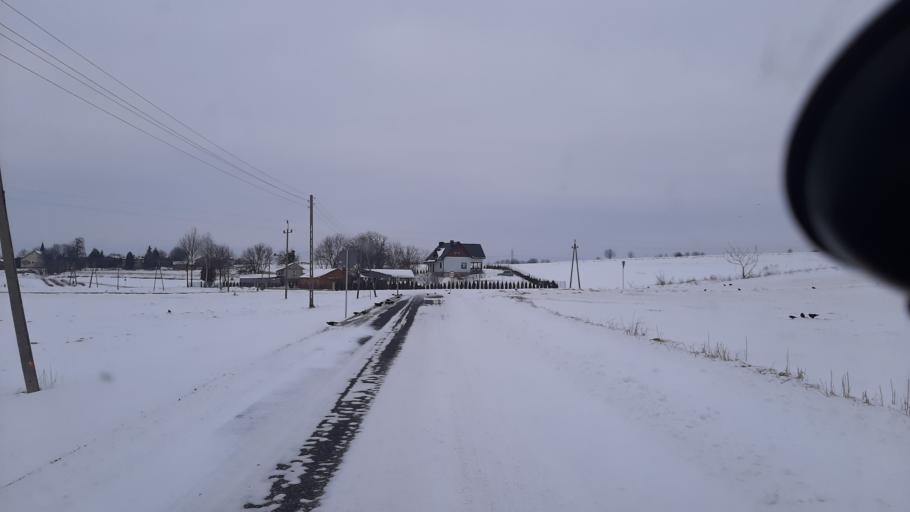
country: PL
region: Lublin Voivodeship
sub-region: Powiat lubelski
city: Garbow
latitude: 51.3388
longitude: 22.2943
